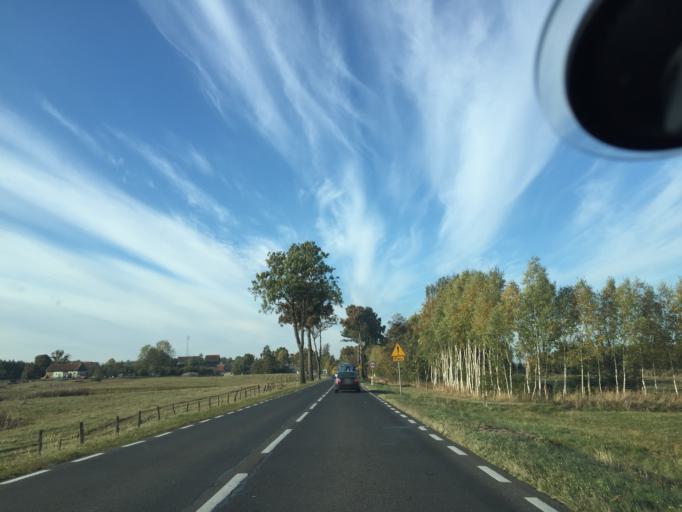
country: PL
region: Warmian-Masurian Voivodeship
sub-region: Powiat bartoszycki
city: Bartoszyce
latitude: 54.1904
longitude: 20.7239
